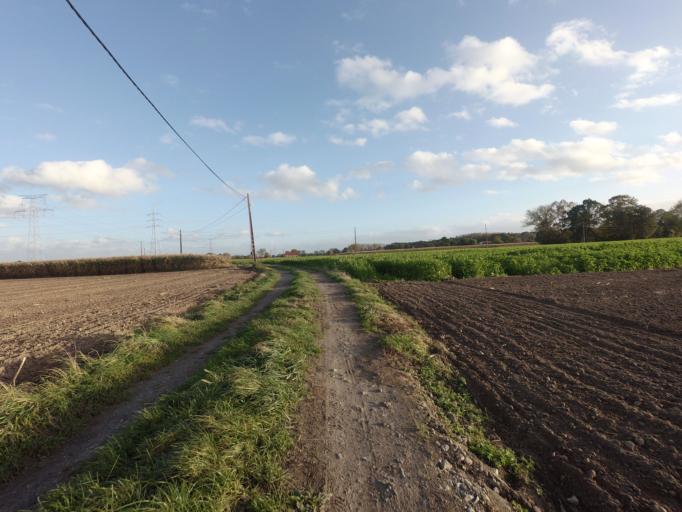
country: BE
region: Flanders
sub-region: Provincie Vlaams-Brabant
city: Zemst
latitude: 50.9778
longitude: 4.4128
